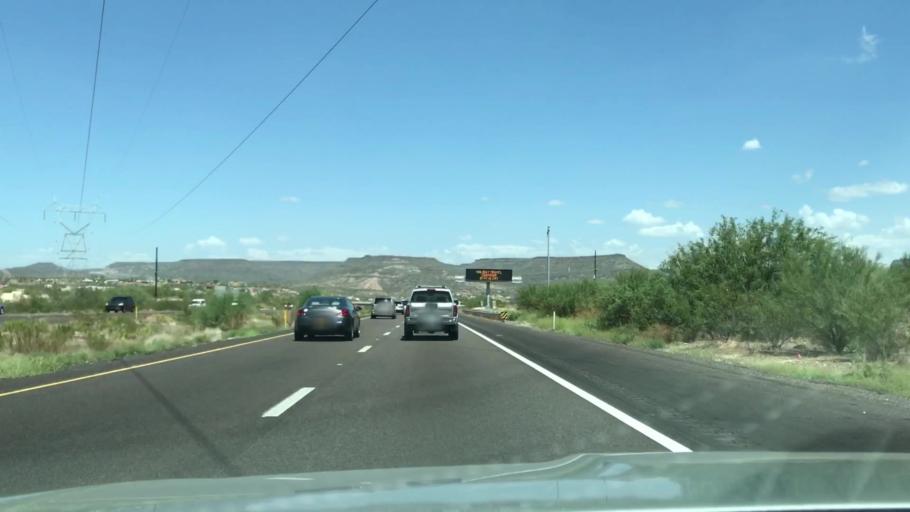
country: US
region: Arizona
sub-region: Yavapai County
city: Black Canyon City
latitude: 34.0605
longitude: -112.1442
